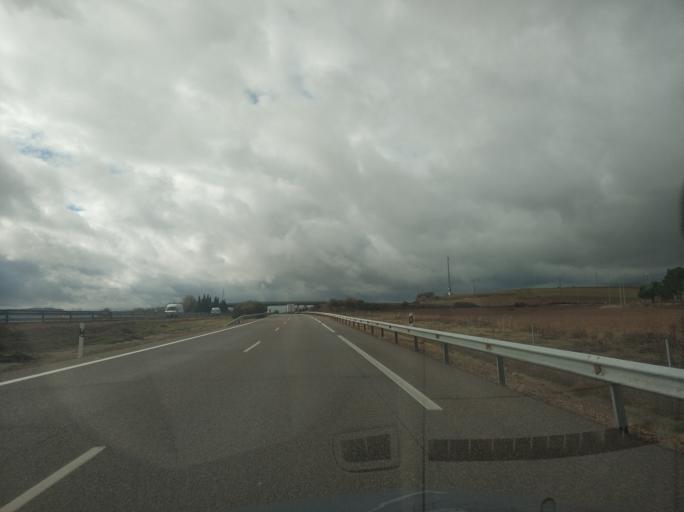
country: ES
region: Castille and Leon
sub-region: Provincia de Palencia
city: Torquemada
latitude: 42.0197
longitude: -4.3392
